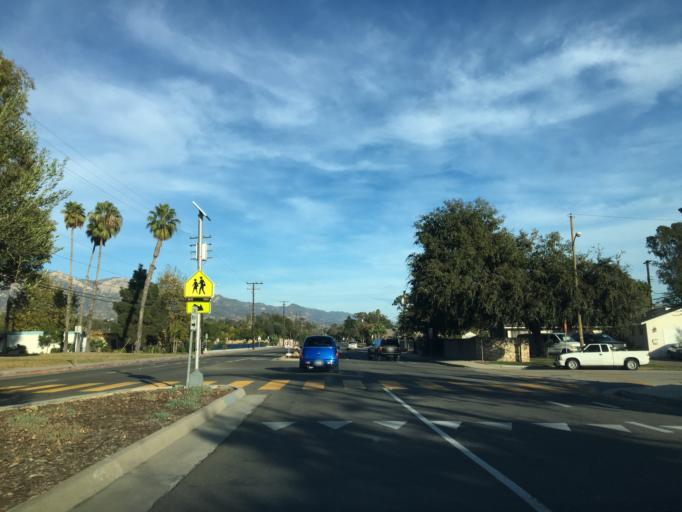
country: US
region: California
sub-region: Santa Barbara County
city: Goleta
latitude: 34.4369
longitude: -119.7874
